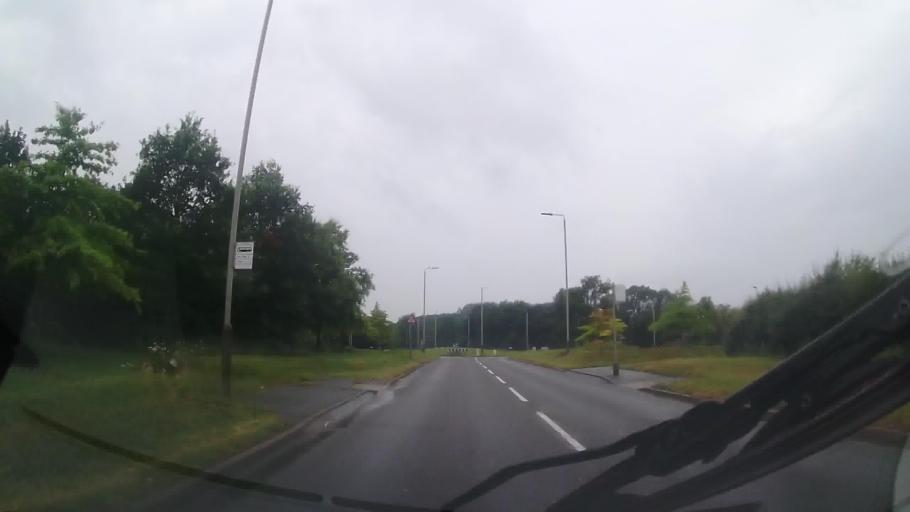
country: GB
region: England
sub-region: Leicestershire
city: Anstey
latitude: 52.6749
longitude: -1.1510
